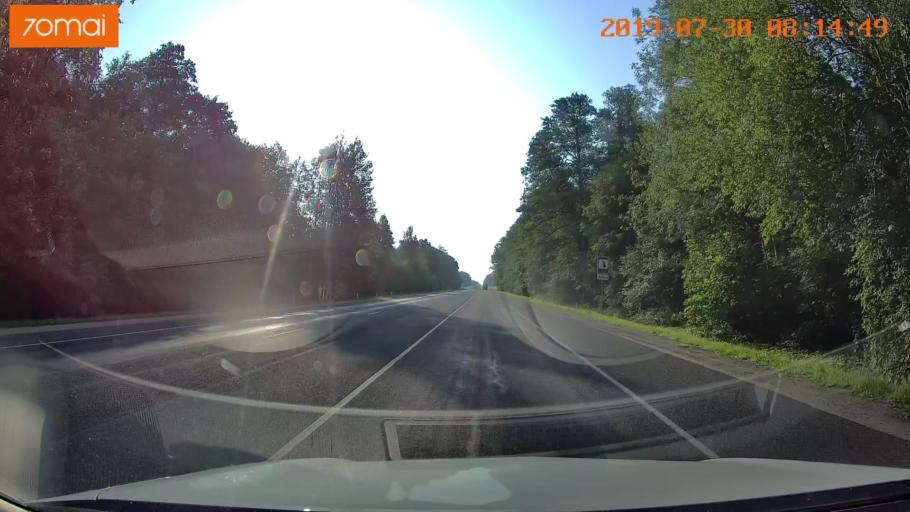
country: RU
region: Kaliningrad
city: Zheleznodorozhnyy
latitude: 54.6467
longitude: 21.3678
